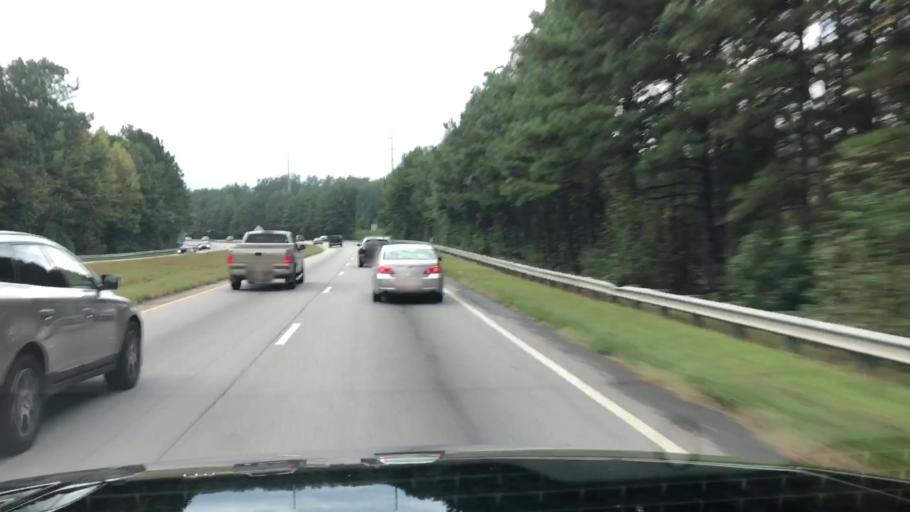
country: US
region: Georgia
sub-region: Cobb County
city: Mableton
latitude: 33.7539
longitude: -84.5903
